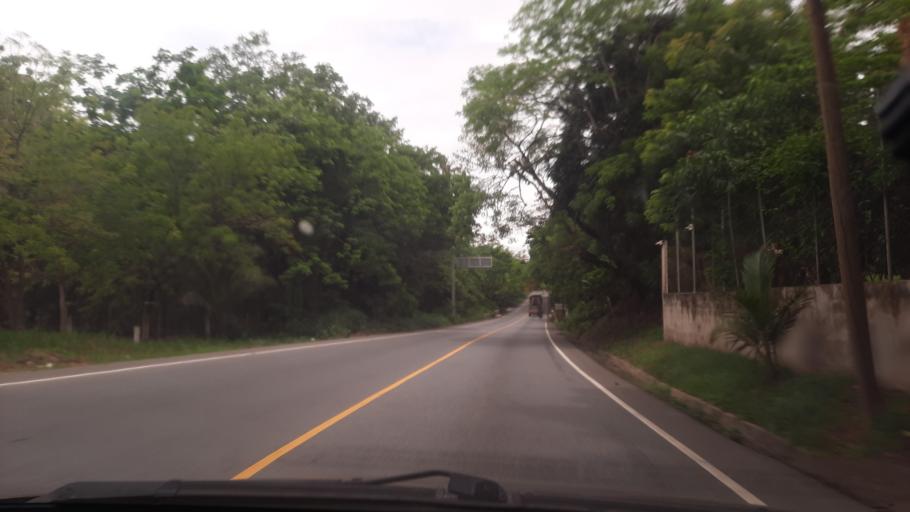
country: GT
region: Izabal
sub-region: Municipio de Los Amates
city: Los Amates
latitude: 15.2220
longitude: -89.2178
